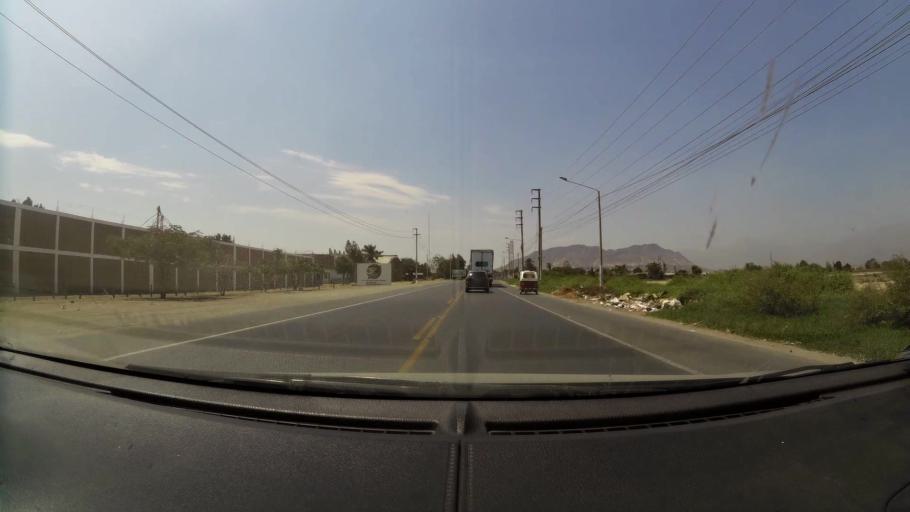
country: PE
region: La Libertad
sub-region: Chepen
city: Chepen
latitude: -7.2338
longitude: -79.4532
